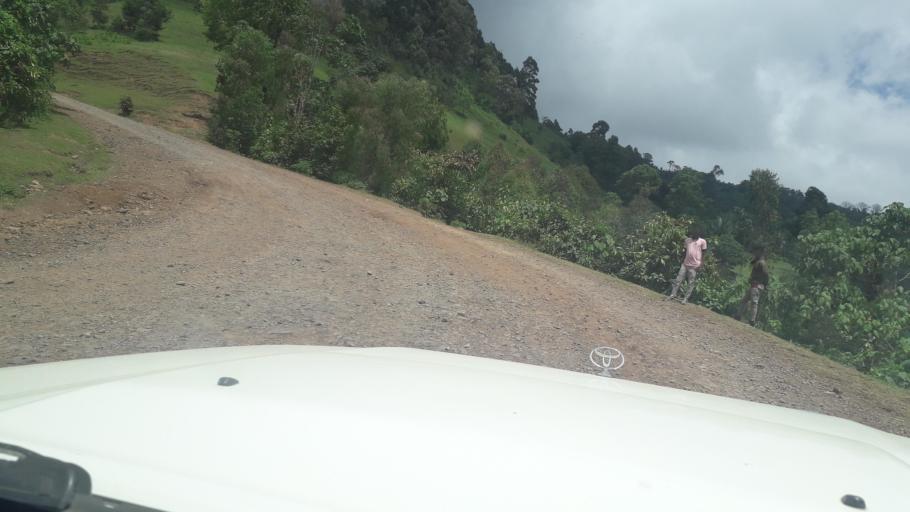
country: ET
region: Oromiya
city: Jima
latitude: 7.4301
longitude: 36.8764
